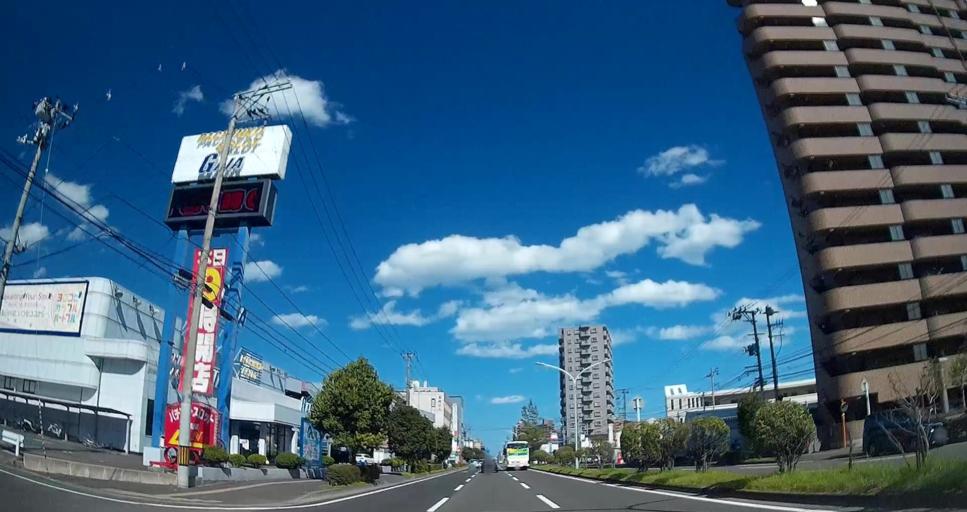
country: JP
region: Miyagi
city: Sendai-shi
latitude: 38.2518
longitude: 140.9159
